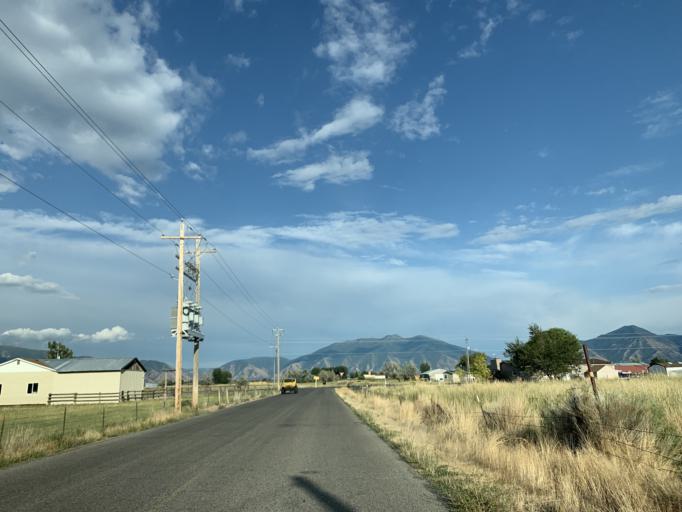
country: US
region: Utah
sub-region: Utah County
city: Benjamin
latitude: 40.1163
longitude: -111.7705
